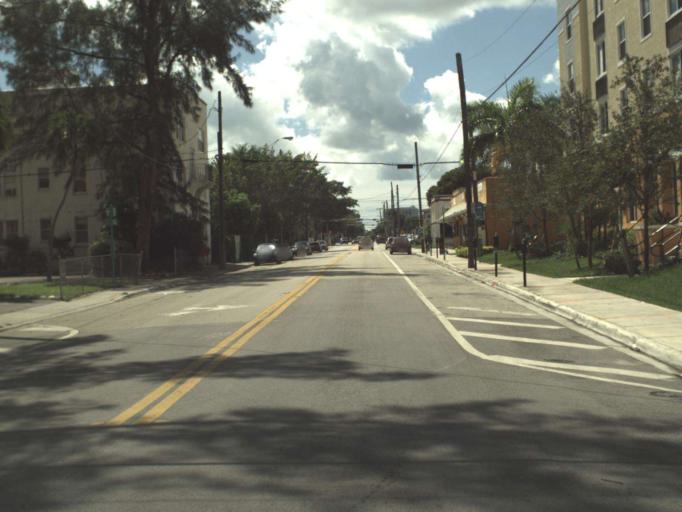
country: US
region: Florida
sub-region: Miami-Dade County
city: Miami
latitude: 25.7699
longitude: -80.2076
